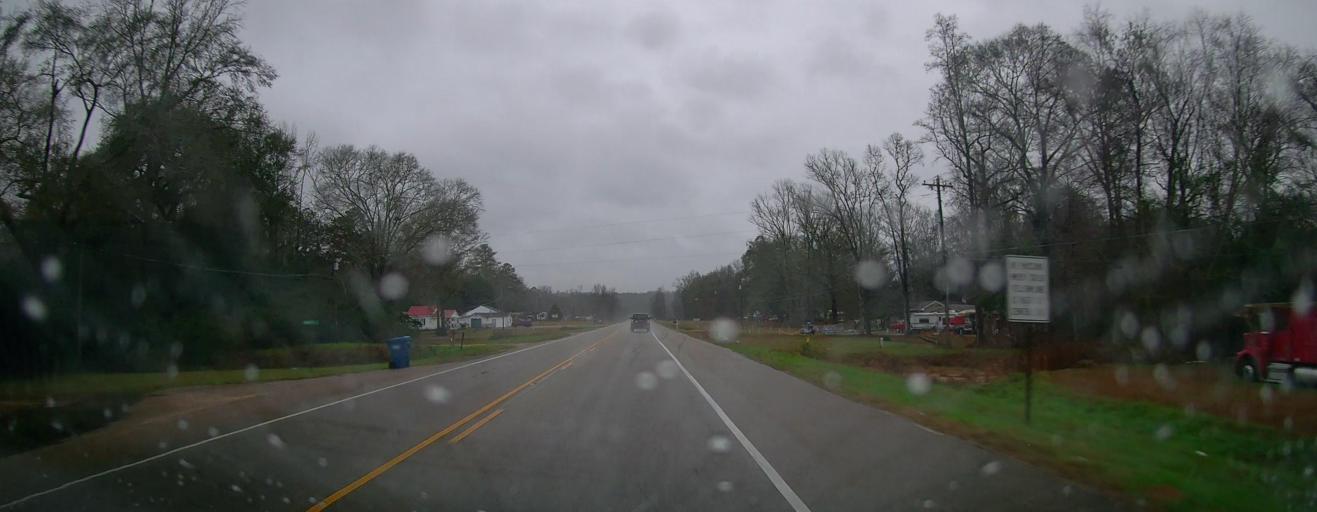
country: US
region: Alabama
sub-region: Autauga County
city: Prattville
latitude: 32.4699
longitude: -86.5074
